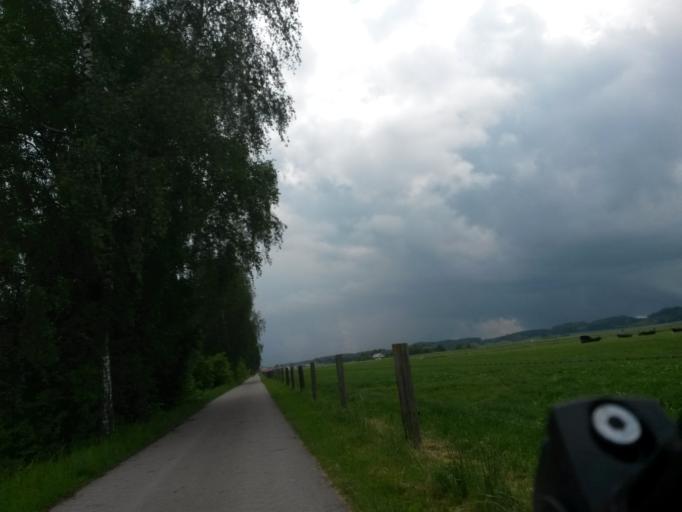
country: DE
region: Baden-Wuerttemberg
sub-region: Tuebingen Region
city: Bad Waldsee
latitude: 47.9358
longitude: 9.8117
